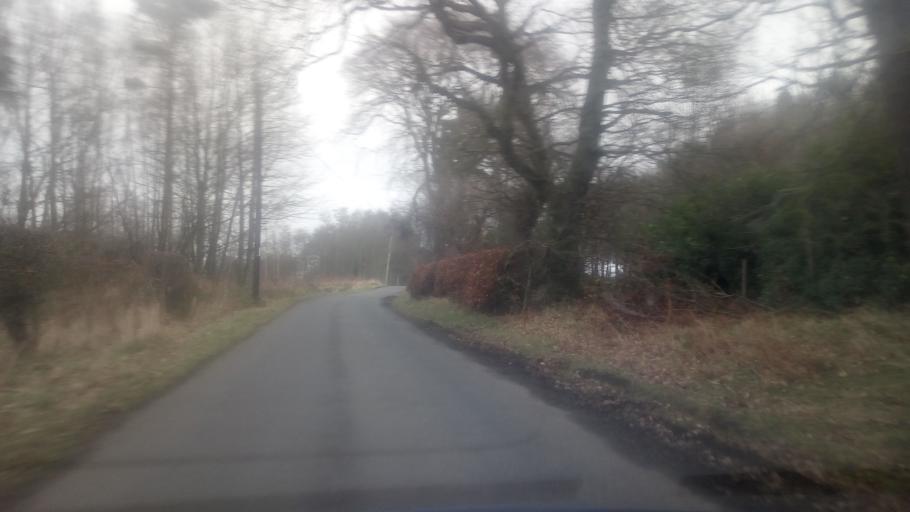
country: GB
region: Scotland
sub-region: The Scottish Borders
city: Jedburgh
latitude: 55.5331
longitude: -2.5027
